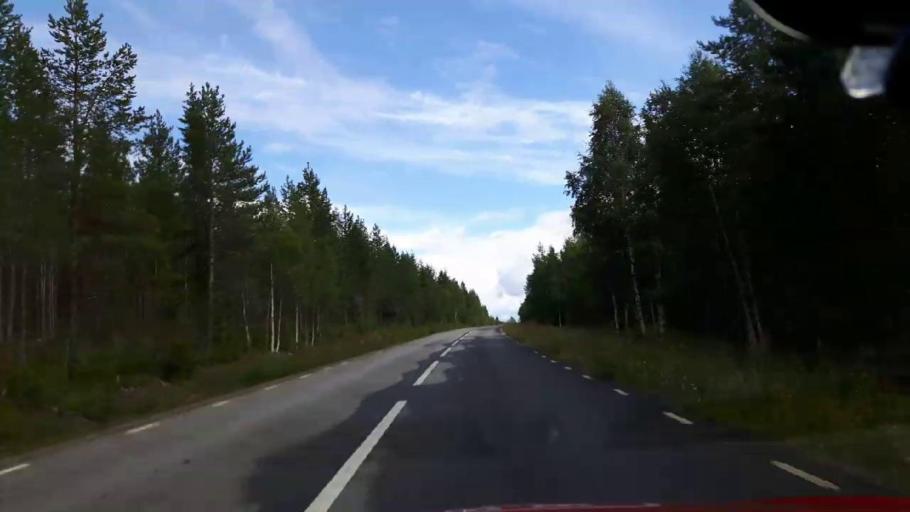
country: SE
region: Jaemtland
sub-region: Stroemsunds Kommun
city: Stroemsund
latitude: 64.3466
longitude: 15.0893
